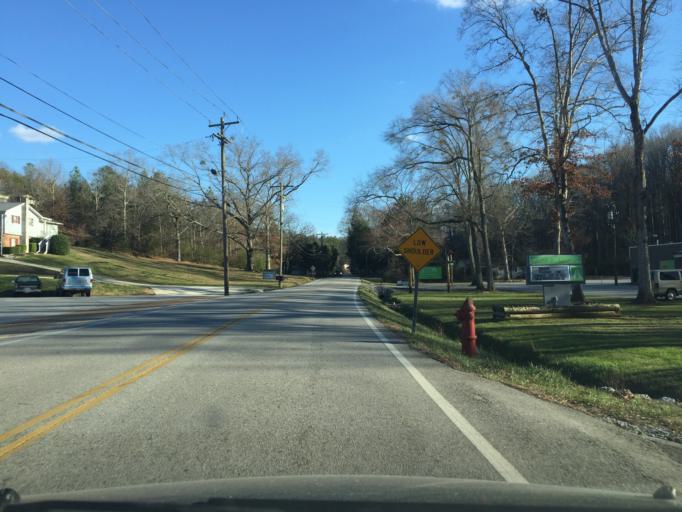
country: US
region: Tennessee
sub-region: Hamilton County
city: Harrison
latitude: 35.1358
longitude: -85.1162
